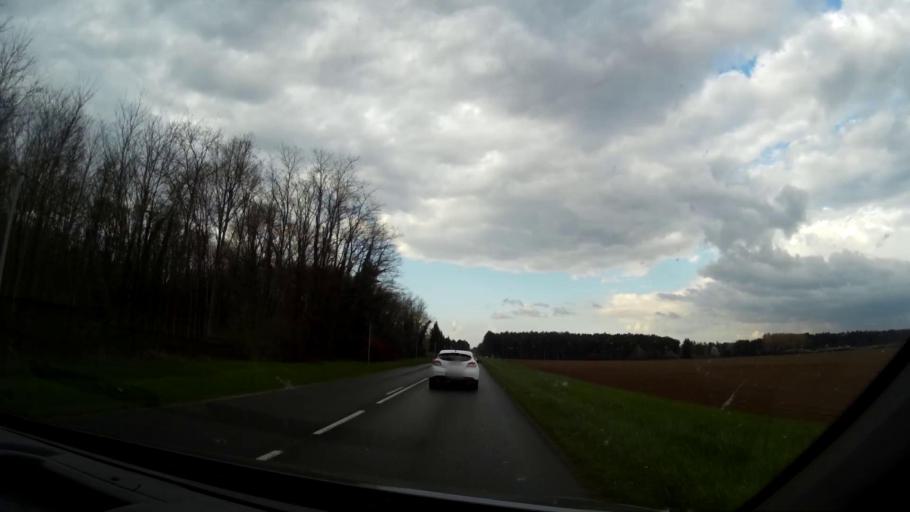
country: FR
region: Centre
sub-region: Departement du Loir-et-Cher
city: Contres
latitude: 47.4514
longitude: 1.4260
